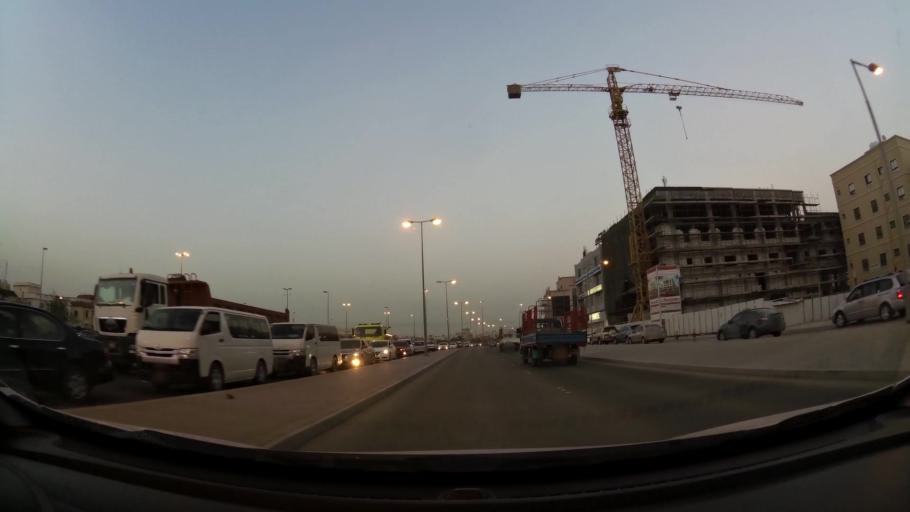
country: BH
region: Manama
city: Jidd Hafs
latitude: 26.2020
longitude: 50.5616
